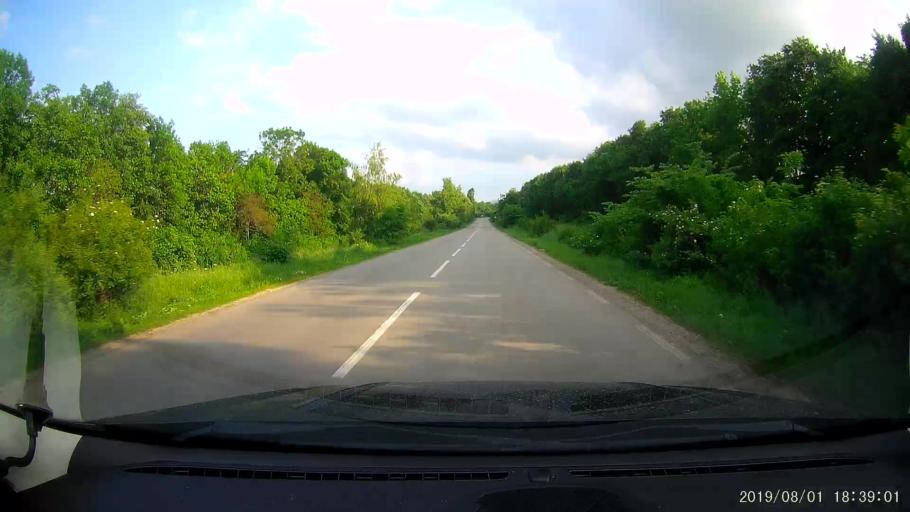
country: BG
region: Shumen
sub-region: Obshtina Khitrino
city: Gara Khitrino
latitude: 43.3940
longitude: 26.9173
